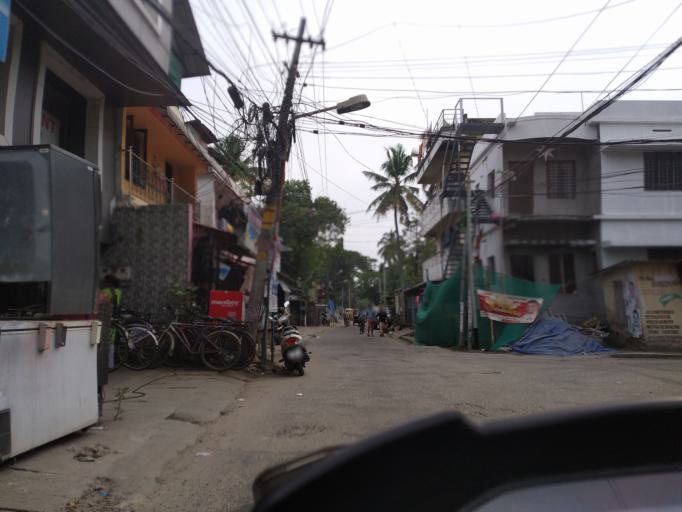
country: IN
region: Kerala
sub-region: Ernakulam
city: Cochin
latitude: 9.9486
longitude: 76.2947
